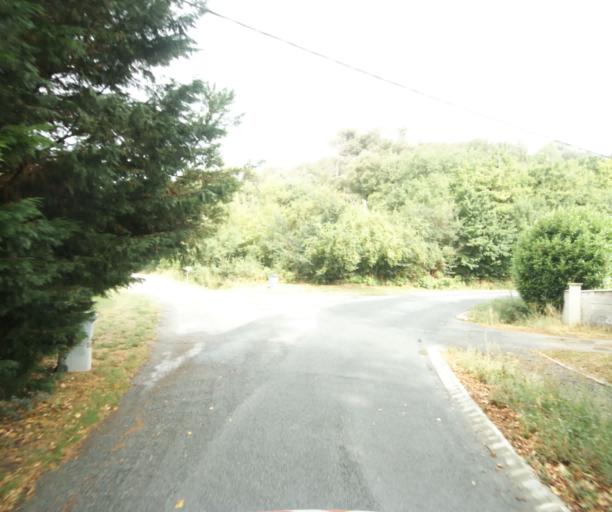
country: FR
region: Midi-Pyrenees
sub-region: Departement de la Haute-Garonne
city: Revel
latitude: 43.4267
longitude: 1.9802
